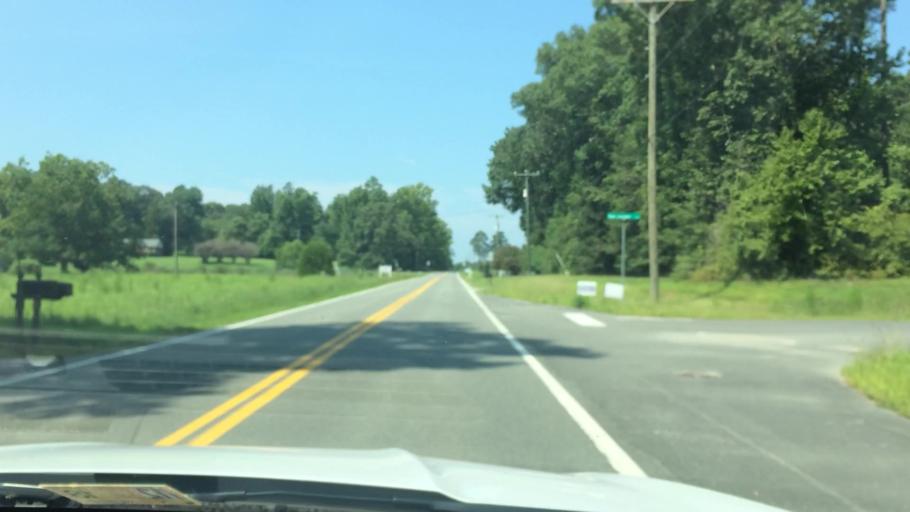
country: US
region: Virginia
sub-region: New Kent County
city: New Kent
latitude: 37.5260
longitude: -77.0363
